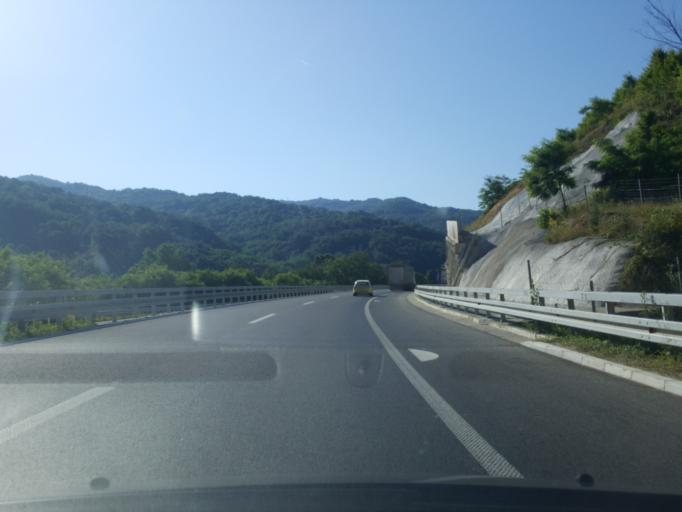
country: RS
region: Central Serbia
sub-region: Jablanicki Okrug
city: Vlasotince
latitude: 42.8540
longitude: 22.1243
